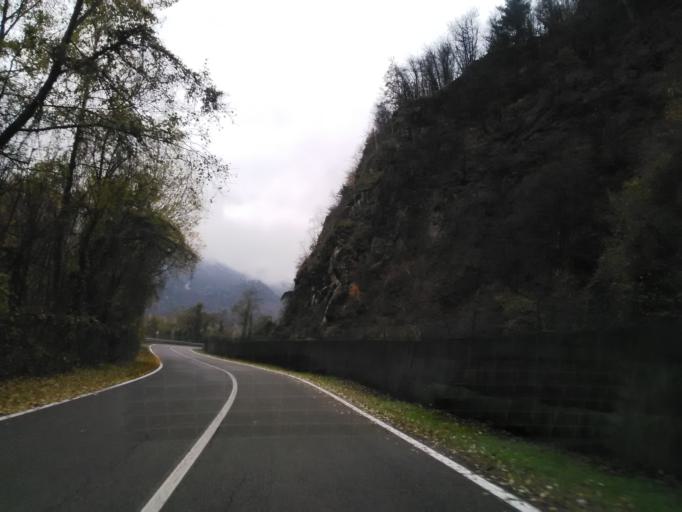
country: IT
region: Piedmont
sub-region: Provincia di Vercelli
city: Varallo
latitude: 45.7999
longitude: 8.2622
